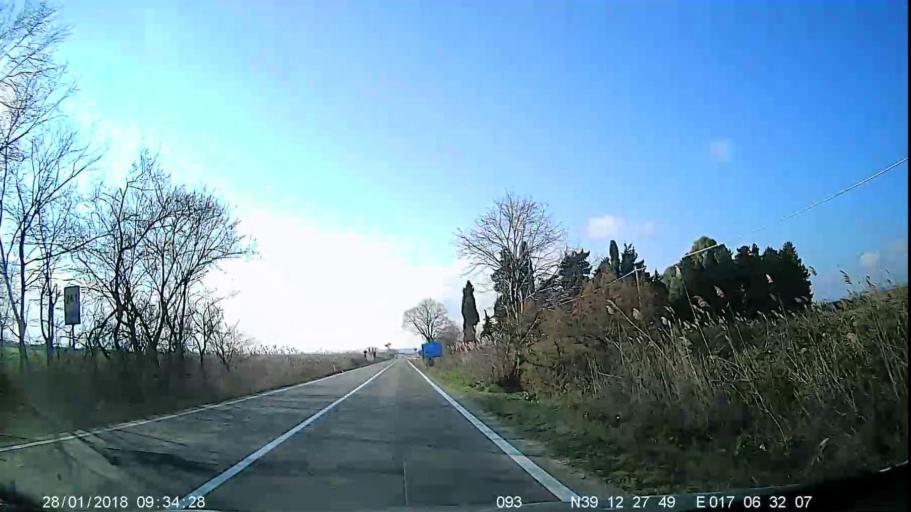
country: IT
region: Calabria
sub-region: Provincia di Crotone
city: Tronca
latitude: 39.2073
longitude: 17.1088
